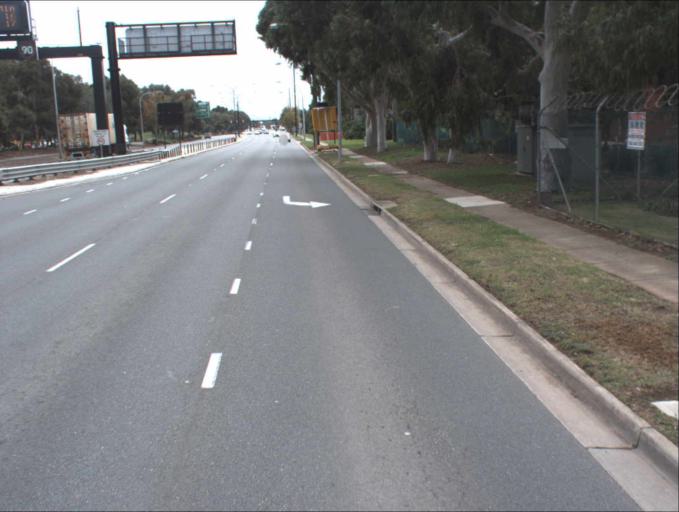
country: AU
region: South Australia
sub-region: Charles Sturt
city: Woodville
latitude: -34.8738
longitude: 138.5713
